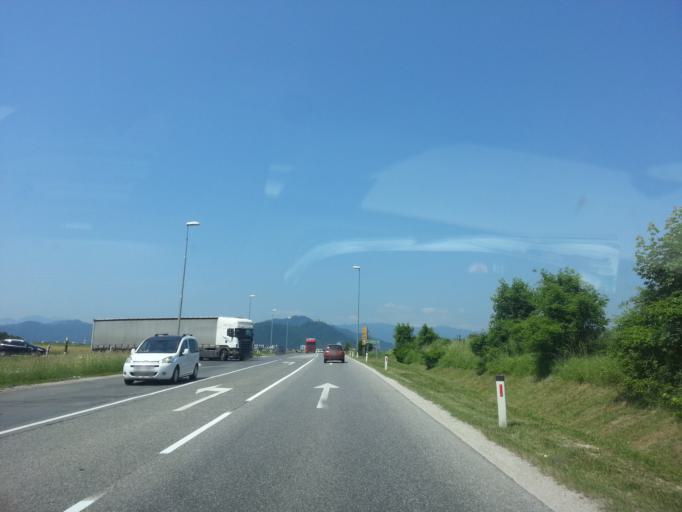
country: SI
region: Kranj
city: Britof
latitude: 46.2415
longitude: 14.3952
